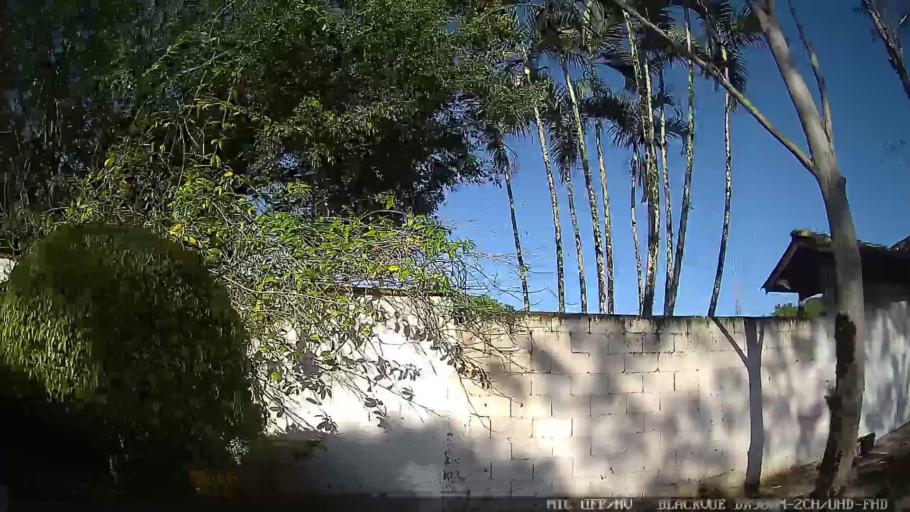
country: BR
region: Sao Paulo
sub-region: Itanhaem
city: Itanhaem
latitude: -24.2111
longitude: -46.8742
